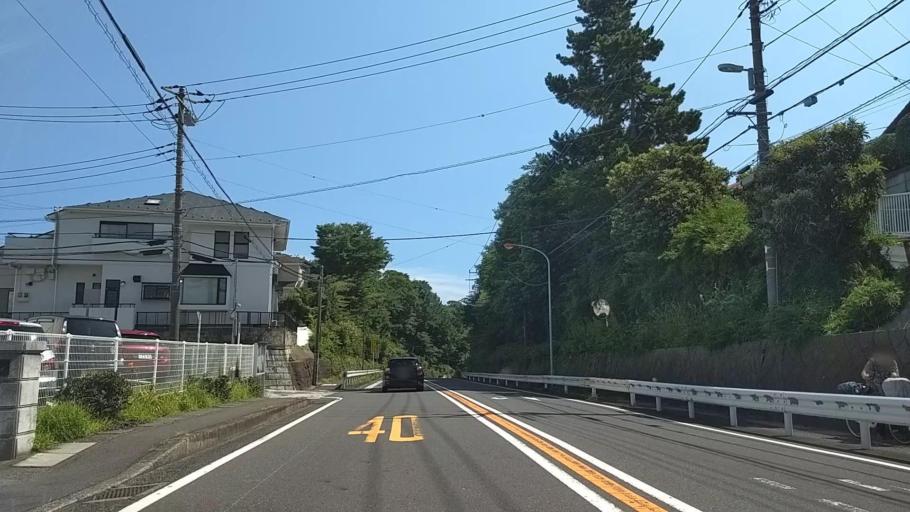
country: JP
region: Kanagawa
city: Fujisawa
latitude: 35.3518
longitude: 139.4908
